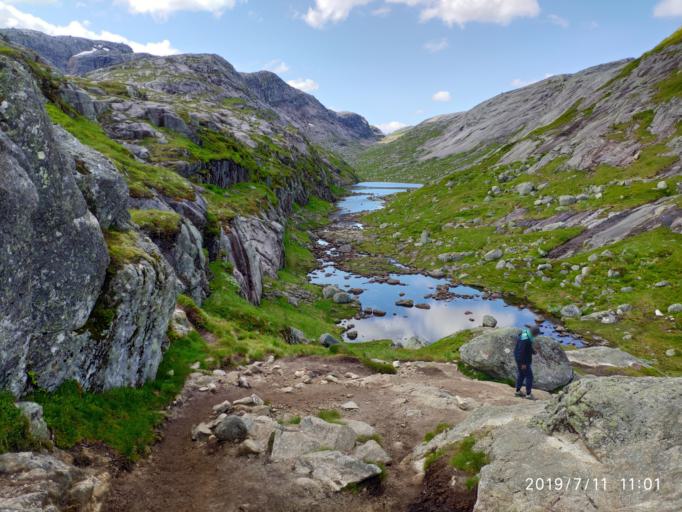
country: NO
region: Vest-Agder
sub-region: Sirdal
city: Tonstad
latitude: 59.0411
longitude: 6.6295
